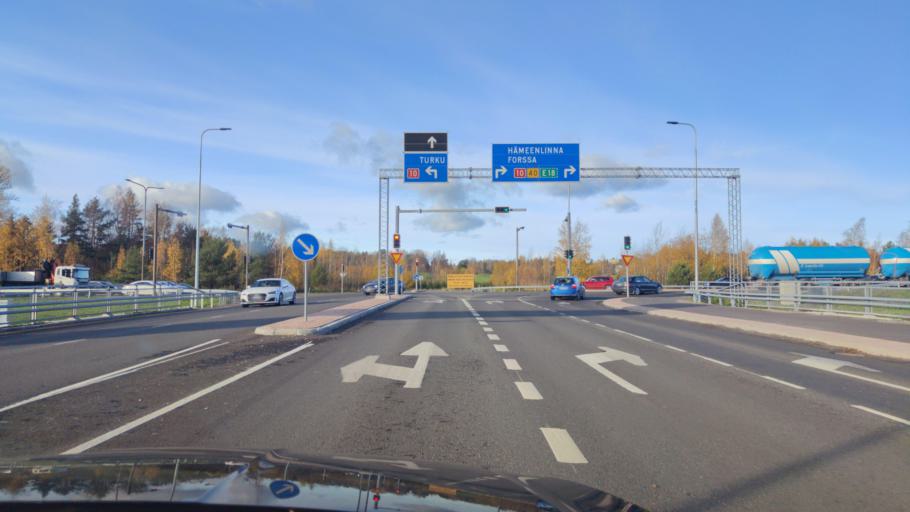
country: FI
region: Varsinais-Suomi
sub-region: Turku
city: Kaarina
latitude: 60.4664
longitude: 22.3481
